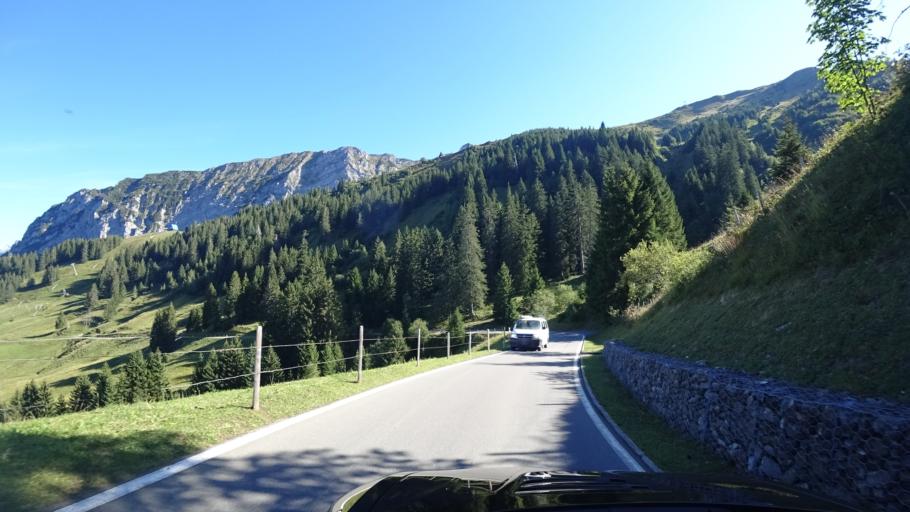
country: CH
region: Obwalden
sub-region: Obwalden
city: Lungern
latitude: 46.8235
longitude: 8.1014
